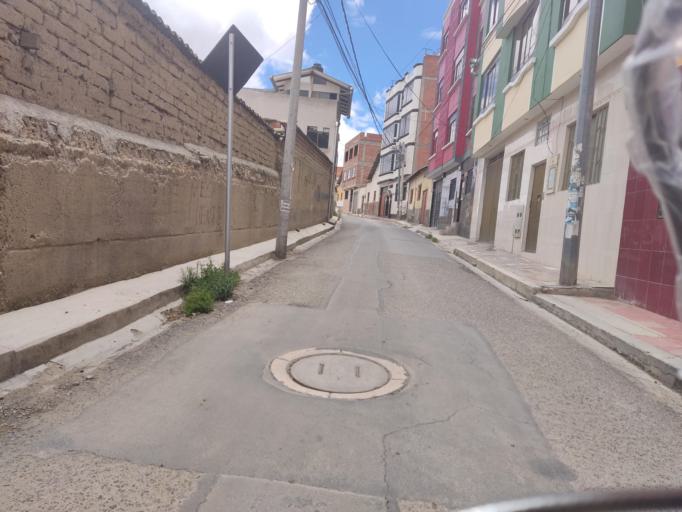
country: BO
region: La Paz
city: La Paz
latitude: -16.4880
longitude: -68.1504
